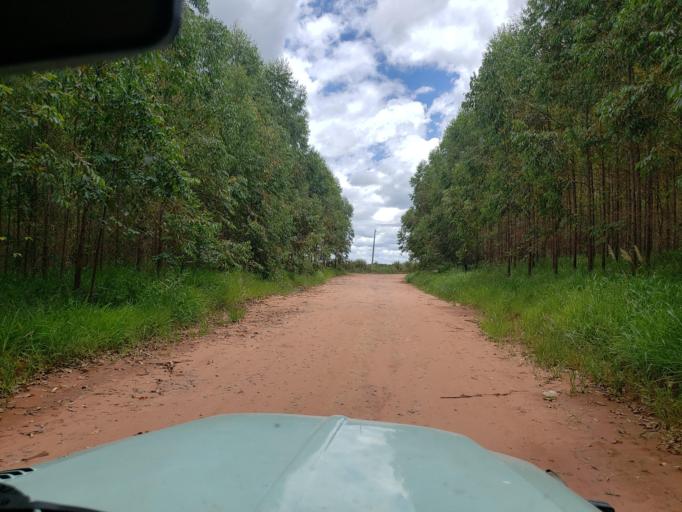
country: BR
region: Sao Paulo
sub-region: Moji-Guacu
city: Mogi-Gaucu
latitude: -22.2238
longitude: -46.8445
